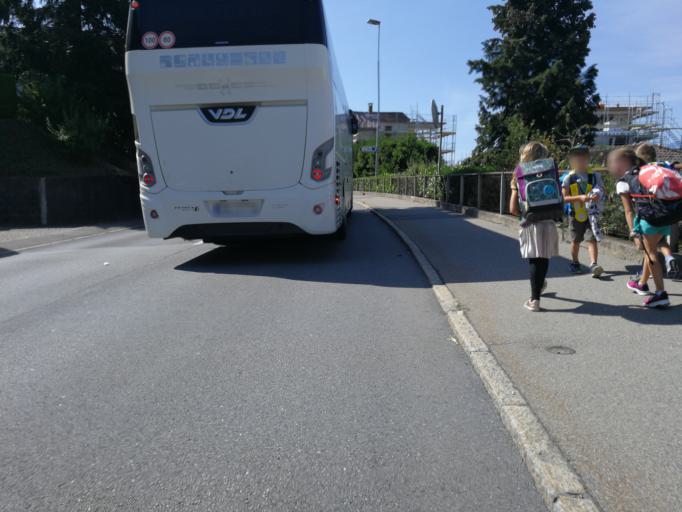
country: CH
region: Schwyz
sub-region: Bezirk Kuessnacht
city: Kussnacht
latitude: 47.0769
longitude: 8.4397
